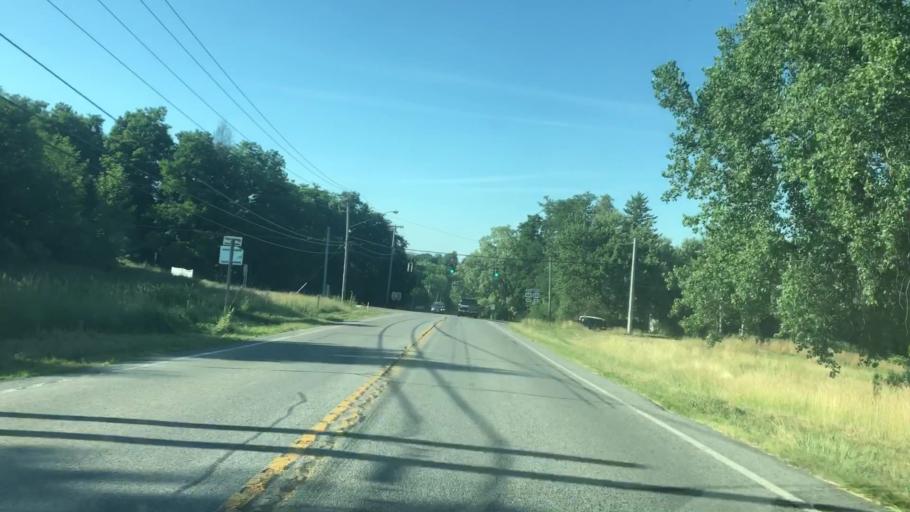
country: US
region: New York
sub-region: Wayne County
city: Macedon
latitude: 43.1383
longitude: -77.2926
